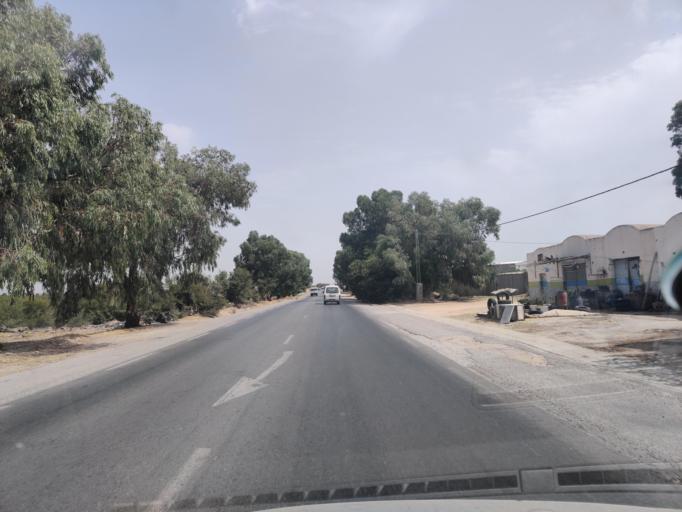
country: TN
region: Nabul
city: Al Hammamat
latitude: 36.4628
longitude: 10.5711
